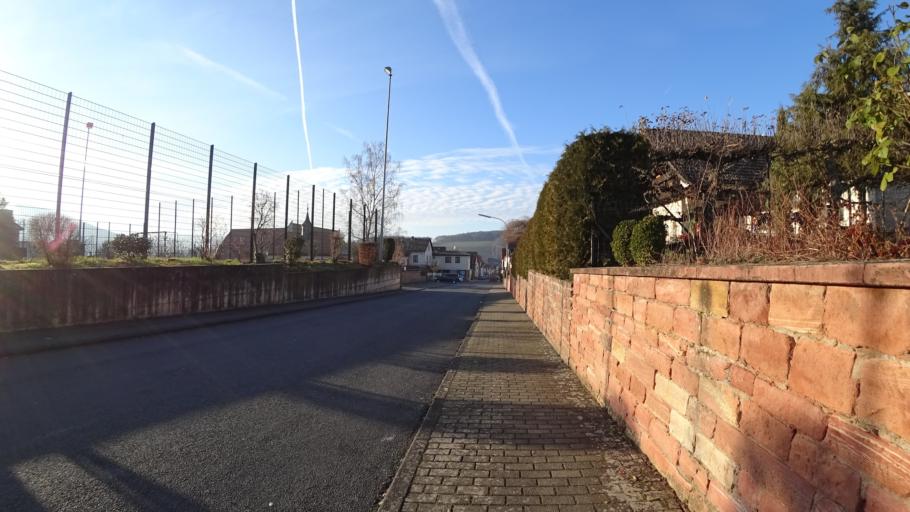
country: DE
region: Bavaria
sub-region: Regierungsbezirk Unterfranken
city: Burgstadt
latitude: 49.7138
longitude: 9.2727
